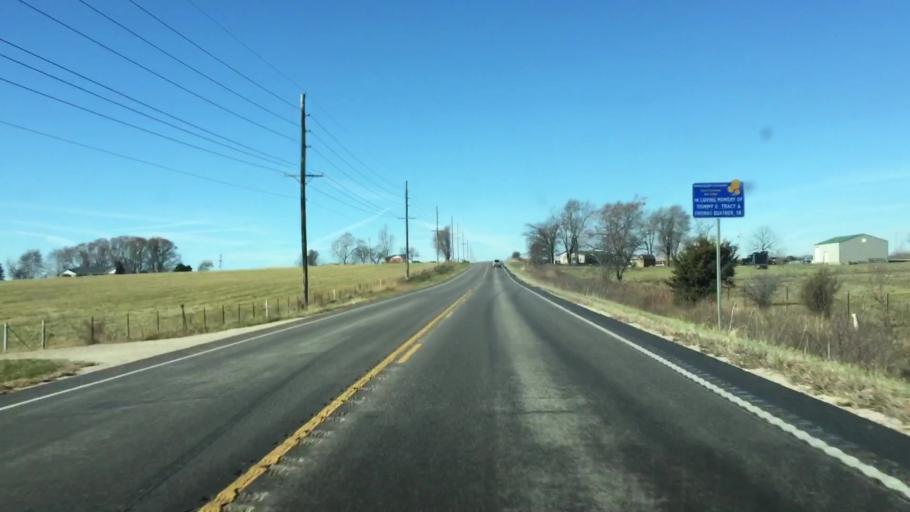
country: US
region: Missouri
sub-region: Miller County
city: Eldon
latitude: 38.3737
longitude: -92.6385
